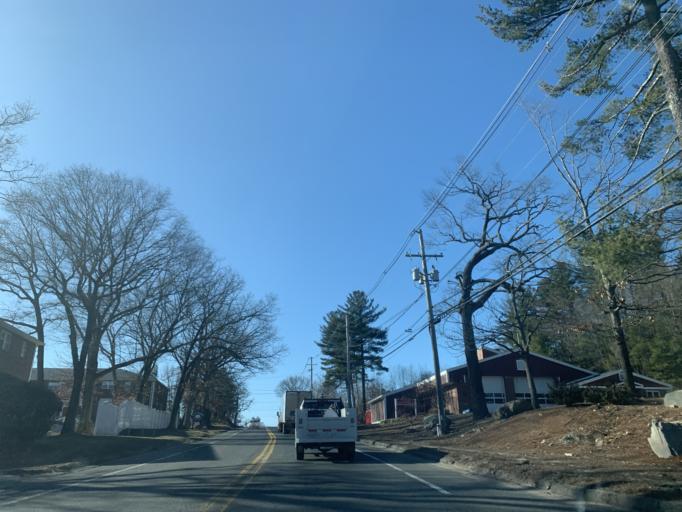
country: US
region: Massachusetts
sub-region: Middlesex County
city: Marlborough
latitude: 42.3496
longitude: -71.5200
